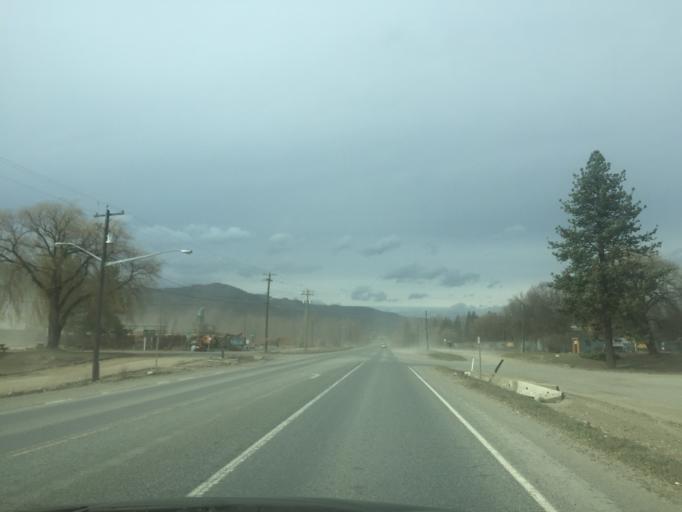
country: CA
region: British Columbia
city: Kamloops
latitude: 51.1740
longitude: -120.1291
